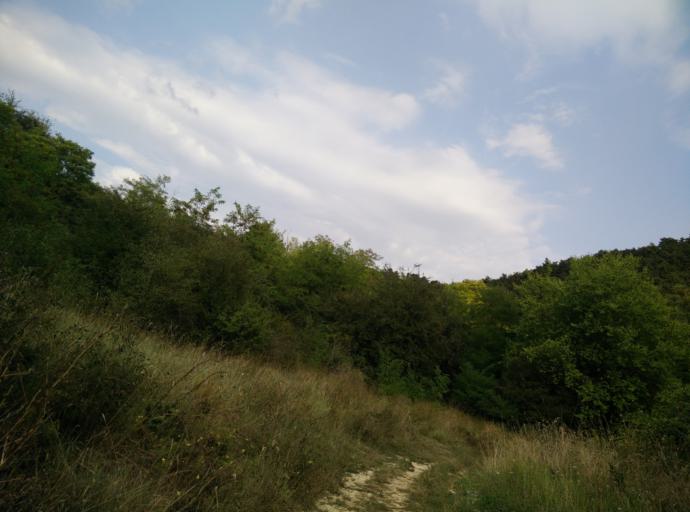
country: HU
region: Pest
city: Paty
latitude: 47.5062
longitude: 18.8456
